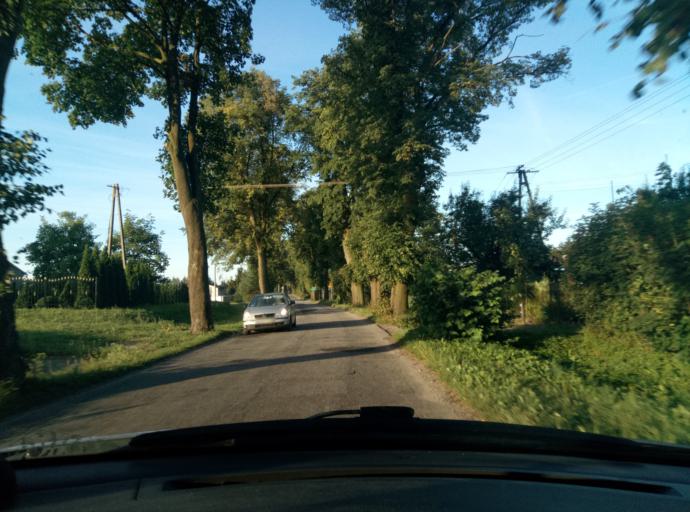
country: PL
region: Kujawsko-Pomorskie
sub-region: Powiat brodnicki
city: Jablonowo Pomorskie
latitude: 53.4036
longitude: 19.1695
